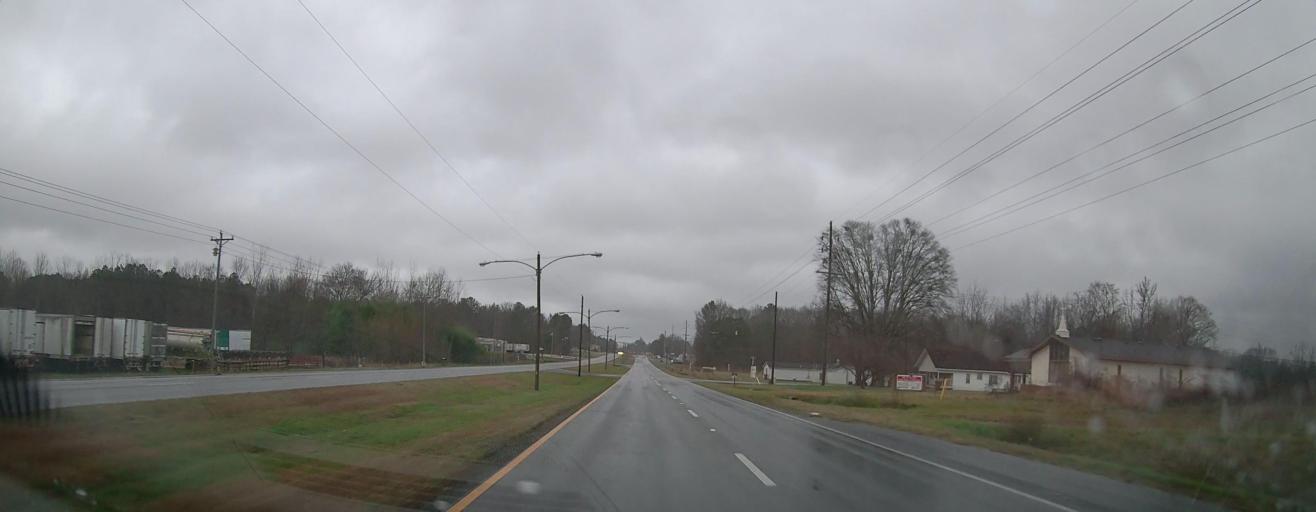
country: US
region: Alabama
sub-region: Morgan County
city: Hartselle
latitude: 34.4181
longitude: -86.9241
